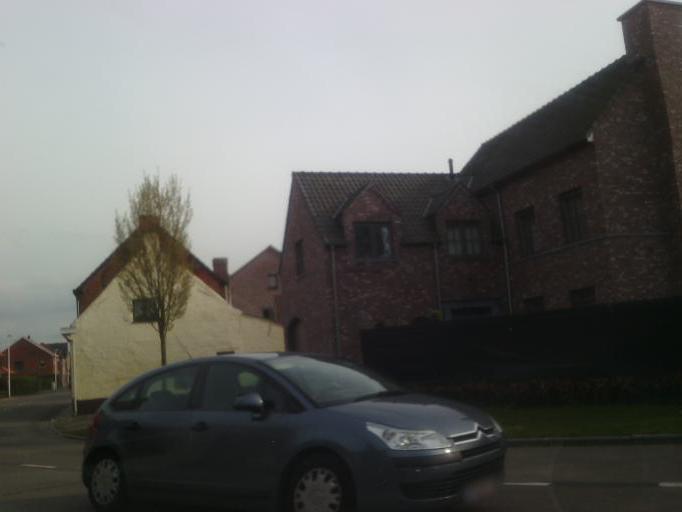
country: BE
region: Flanders
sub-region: Provincie Oost-Vlaanderen
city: Zele
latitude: 51.0680
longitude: 4.0192
